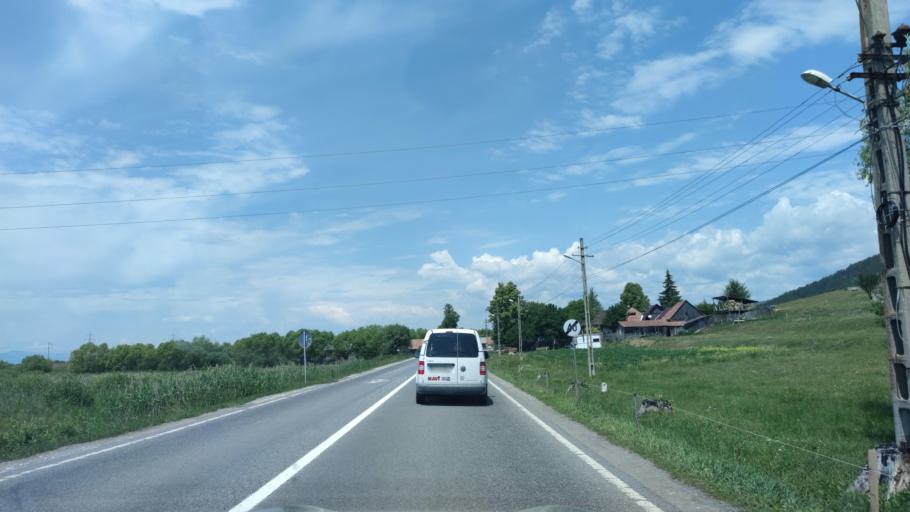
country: RO
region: Harghita
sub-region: Comuna Voslobeni
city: Voslobeni
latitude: 46.6318
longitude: 25.6233
